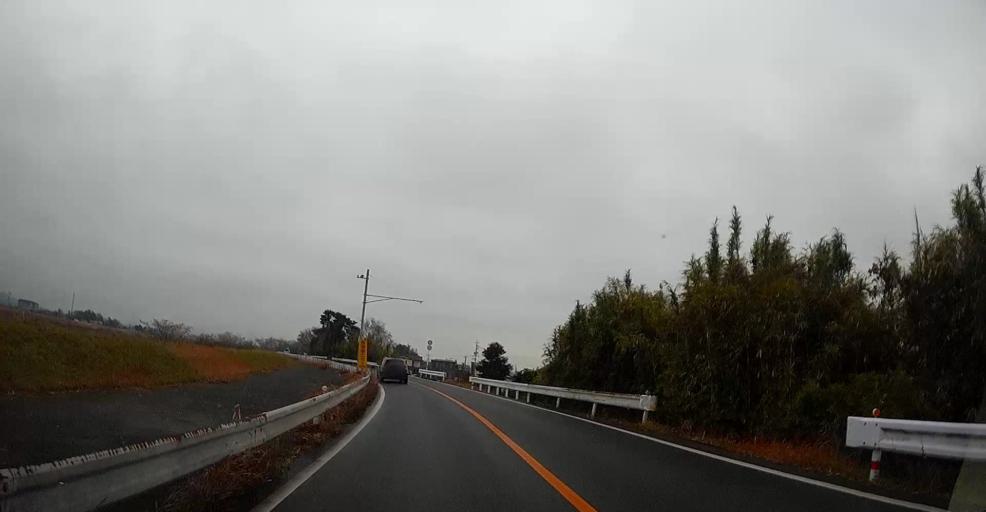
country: JP
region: Kumamoto
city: Kumamoto
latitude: 32.7589
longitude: 130.7513
